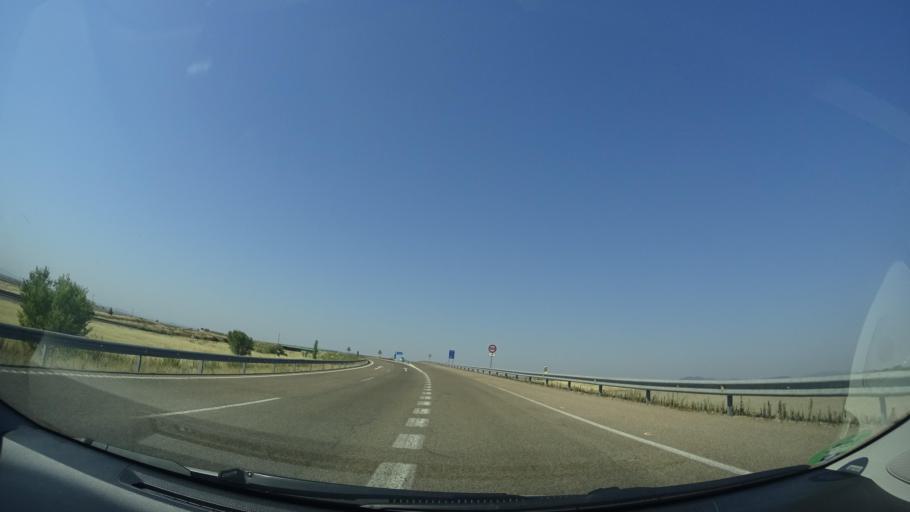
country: ES
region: Extremadura
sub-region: Provincia de Caceres
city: Miajadas
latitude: 39.1284
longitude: -5.9556
